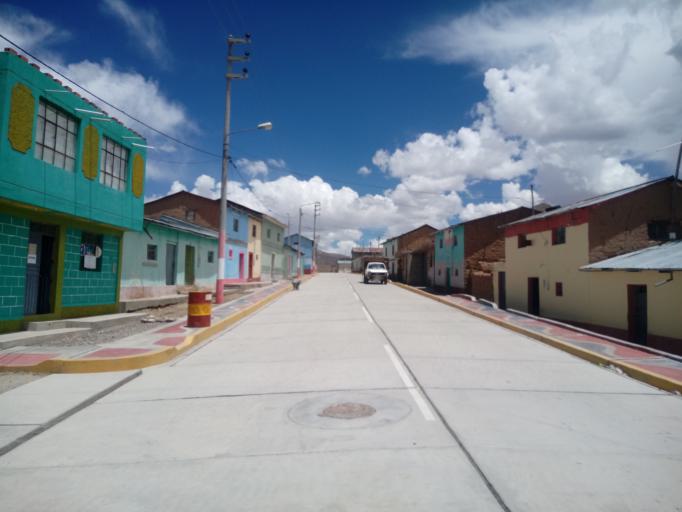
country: PE
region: Puno
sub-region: El Collao
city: Mazo Cruz
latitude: -16.7617
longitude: -69.8542
